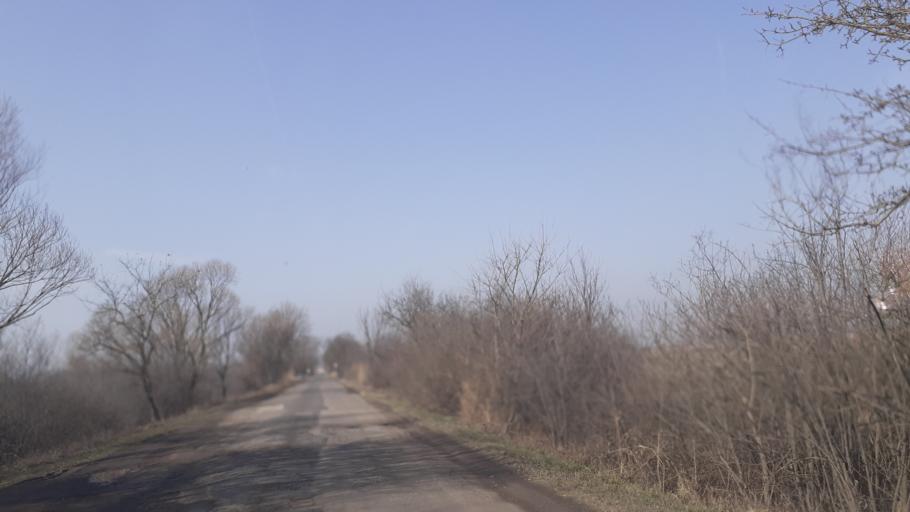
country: HU
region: Pest
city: Dabas
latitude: 47.0602
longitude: 19.2914
